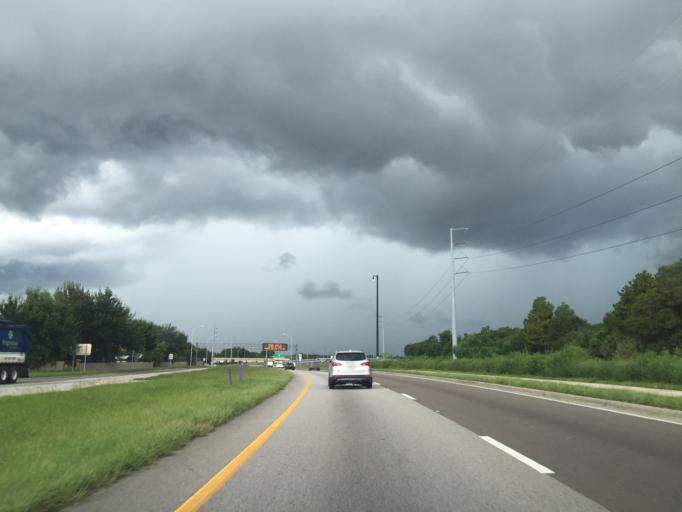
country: US
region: Florida
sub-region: Orange County
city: Lockhart
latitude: 28.6391
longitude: -81.4453
